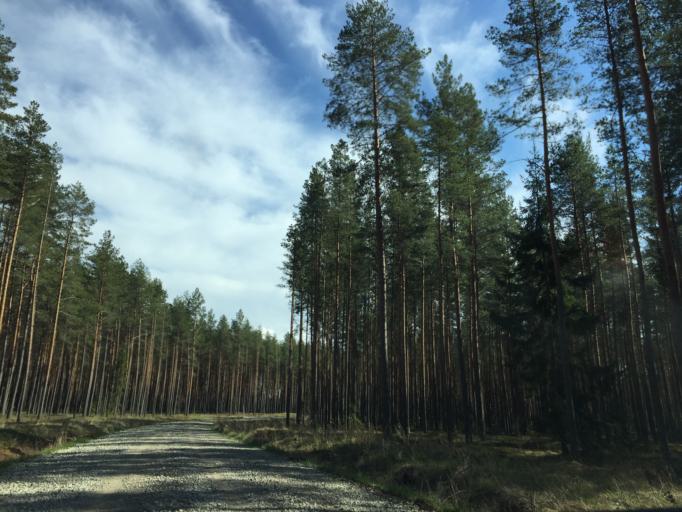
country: LV
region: Strenci
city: Strenci
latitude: 57.5825
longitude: 25.7101
